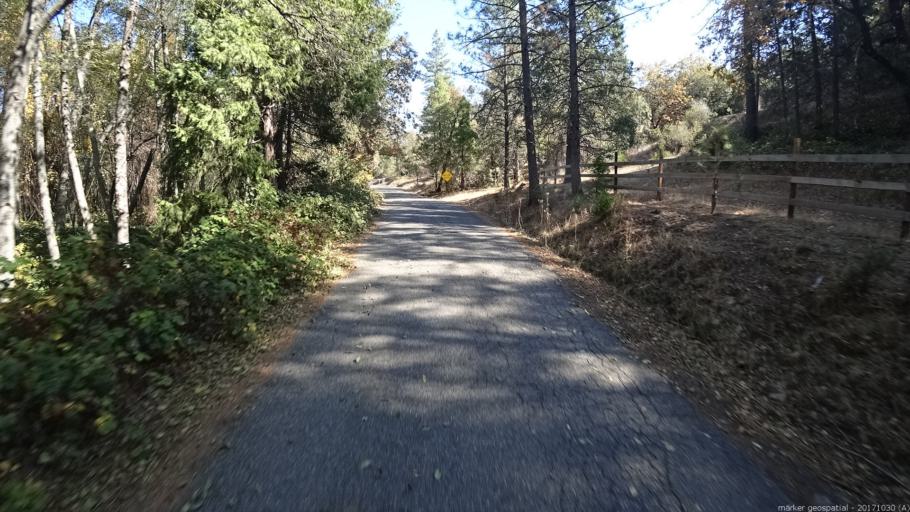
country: US
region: California
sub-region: Shasta County
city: Shingletown
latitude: 40.5680
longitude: -121.8811
